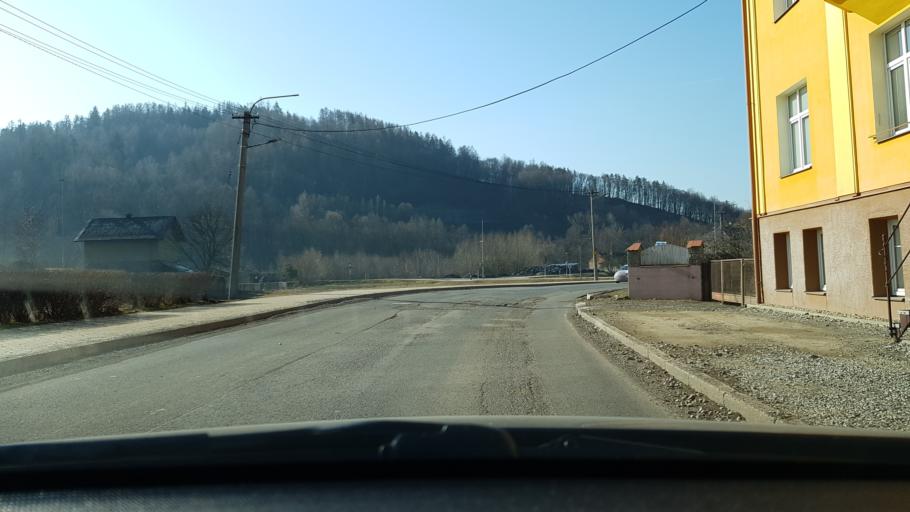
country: CZ
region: Olomoucky
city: Ruda nad Moravou
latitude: 49.9829
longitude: 16.8875
